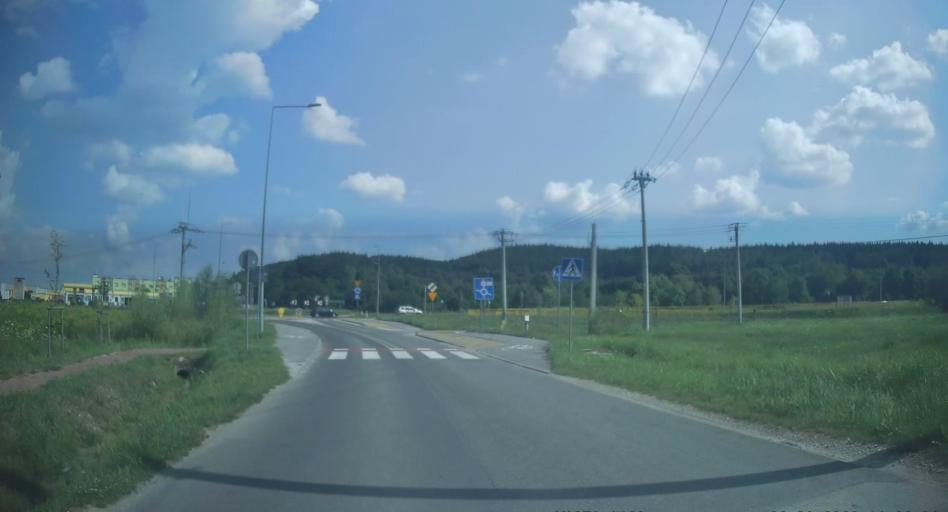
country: PL
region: Swietokrzyskie
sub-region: Powiat kielecki
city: Checiny
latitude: 50.8051
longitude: 20.4456
